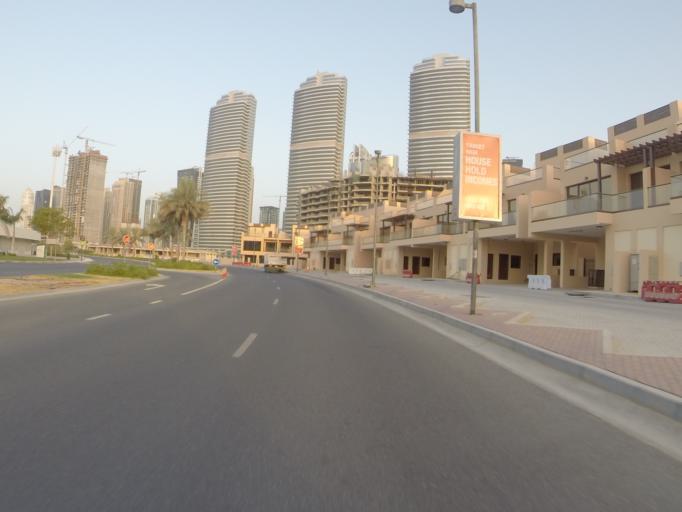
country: AE
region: Dubai
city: Dubai
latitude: 25.0676
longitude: 55.1493
